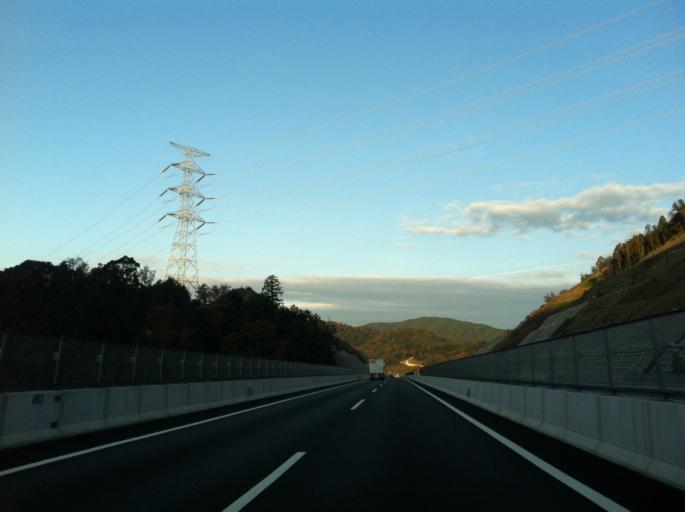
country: JP
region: Aichi
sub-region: Tokai-shi
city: Toyokawa
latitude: 34.8884
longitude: 137.3541
